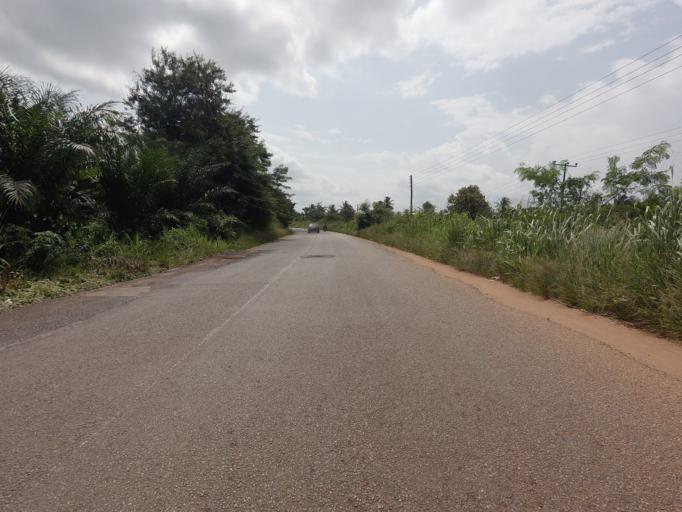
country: TG
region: Maritime
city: Lome
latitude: 6.2195
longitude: 1.0445
